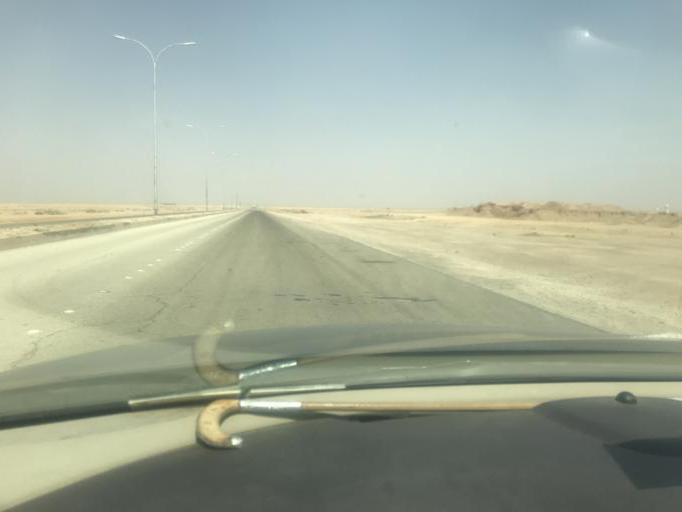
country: SA
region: Ar Riyad
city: Riyadh
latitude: 24.9867
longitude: 46.6875
